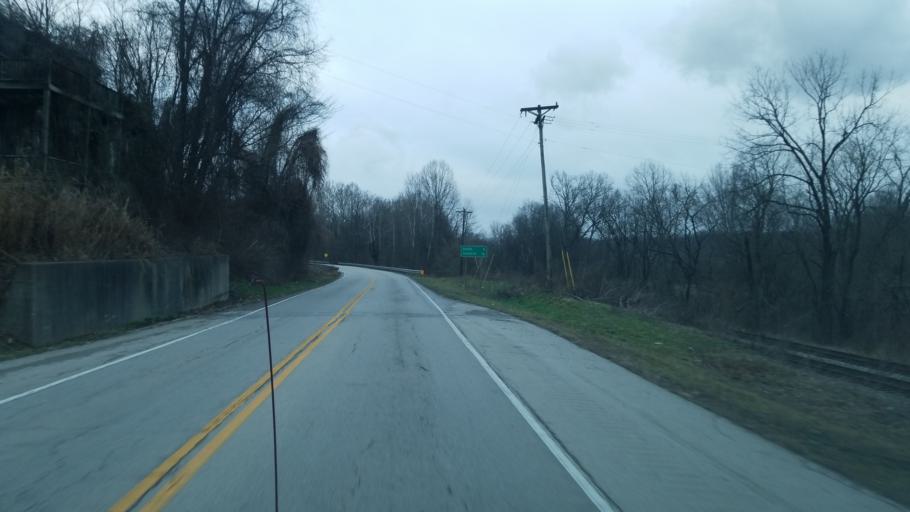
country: US
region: Ohio
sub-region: Brown County
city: Aberdeen
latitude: 38.6868
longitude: -83.7888
